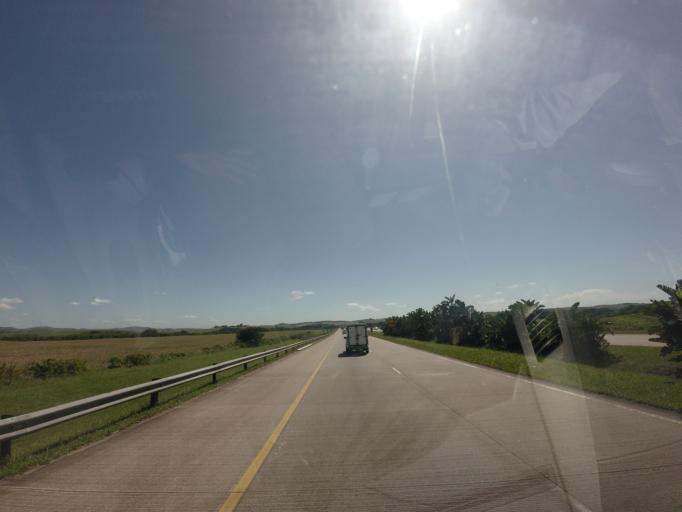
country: ZA
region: KwaZulu-Natal
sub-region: iLembe District Municipality
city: Stanger
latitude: -29.3746
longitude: 31.2986
